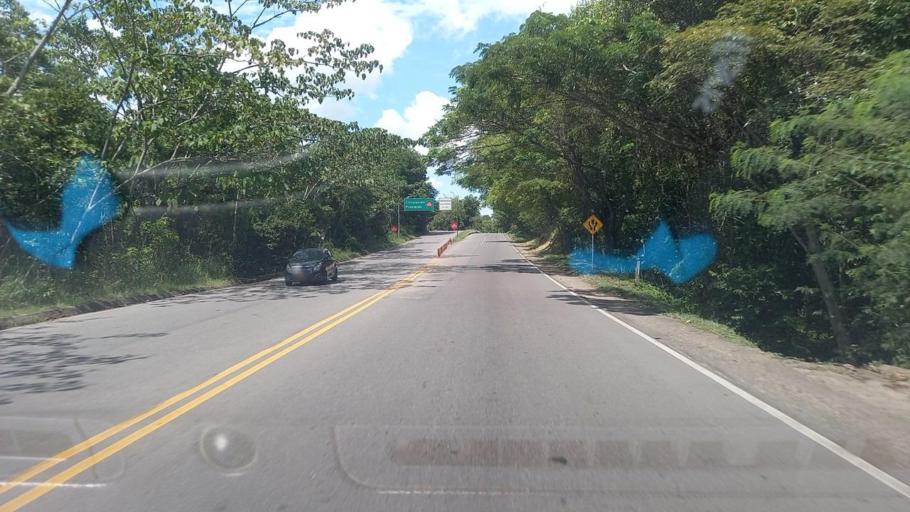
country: CO
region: Santander
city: Barrancabermeja
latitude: 7.1200
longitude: -73.6106
